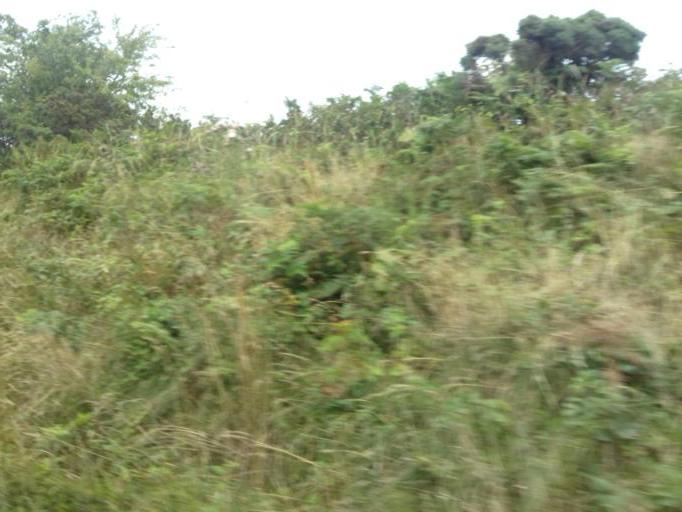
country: IE
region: Leinster
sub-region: Loch Garman
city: Bunclody
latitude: 52.6538
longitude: -6.7450
